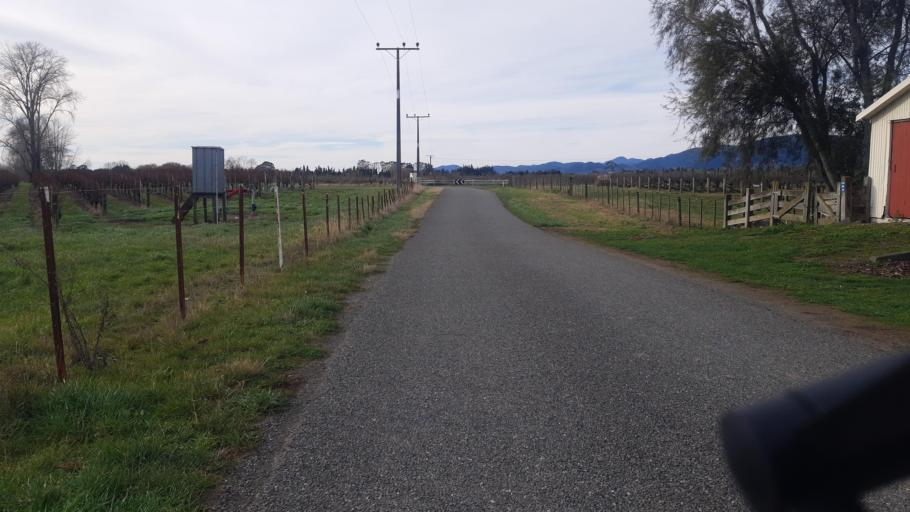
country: NZ
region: Tasman
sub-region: Tasman District
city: Brightwater
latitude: -41.3712
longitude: 173.1111
